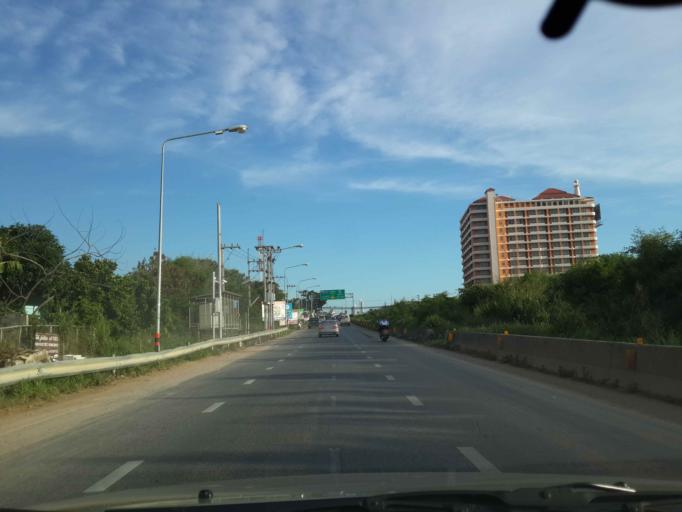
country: TH
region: Chon Buri
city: Phatthaya
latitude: 12.9123
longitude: 100.9018
